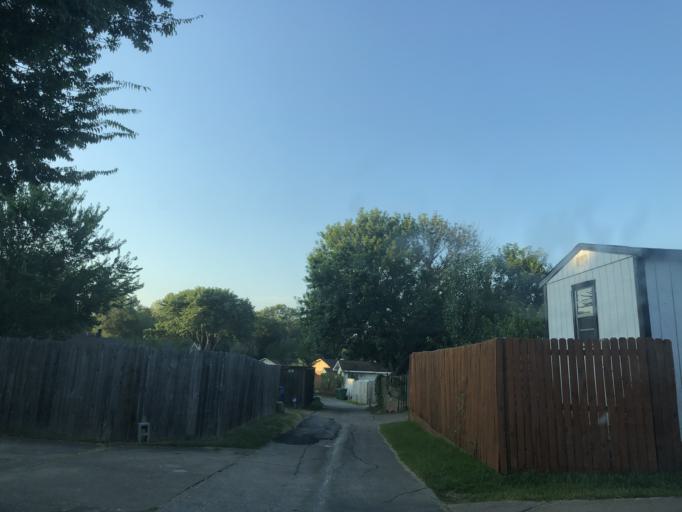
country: US
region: Texas
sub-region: Dallas County
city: Sunnyvale
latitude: 32.8401
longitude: -96.5733
